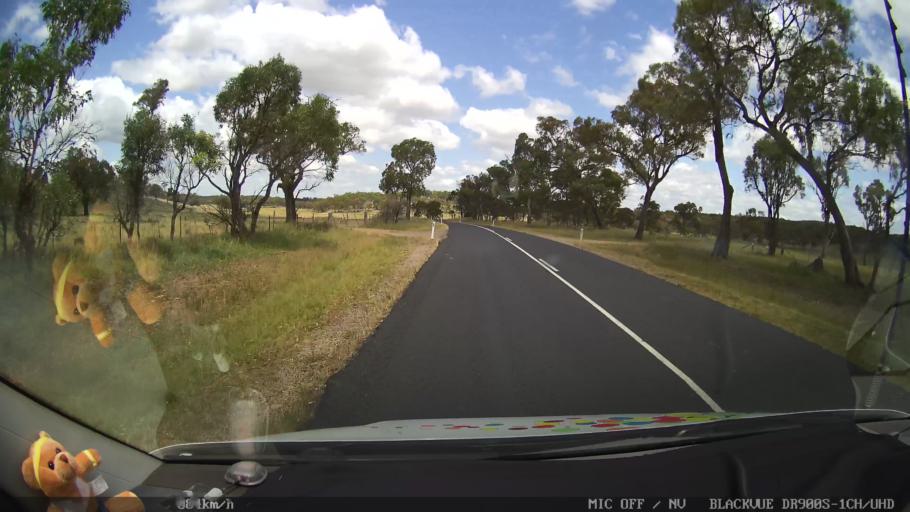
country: AU
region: New South Wales
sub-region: Glen Innes Severn
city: Glen Innes
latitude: -29.4696
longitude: 151.6497
